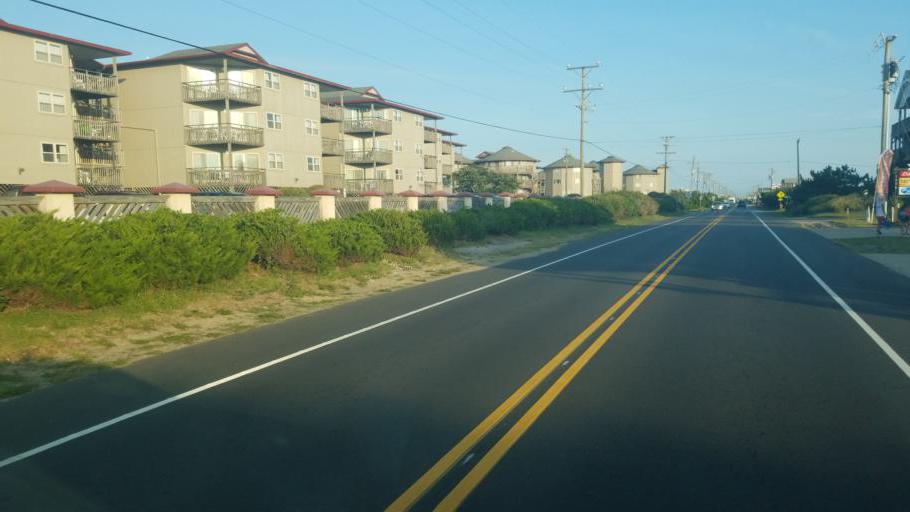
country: US
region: North Carolina
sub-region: Dare County
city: Kill Devil Hills
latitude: 36.0081
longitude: -75.6538
